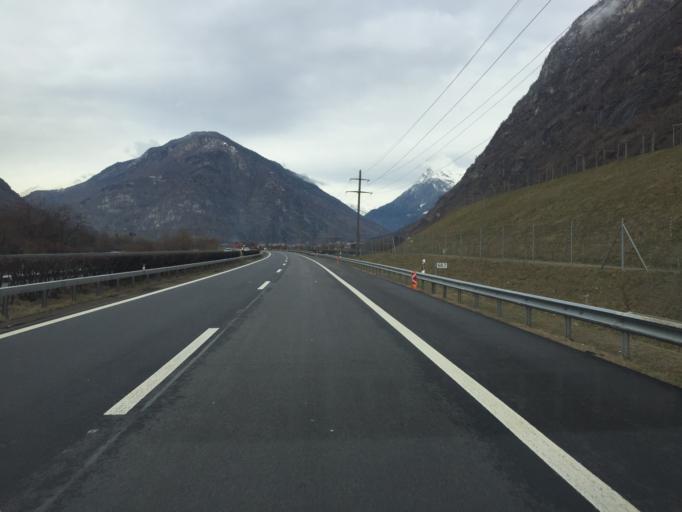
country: CH
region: Ticino
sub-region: Riviera District
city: Lodrino
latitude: 46.3249
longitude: 8.9802
